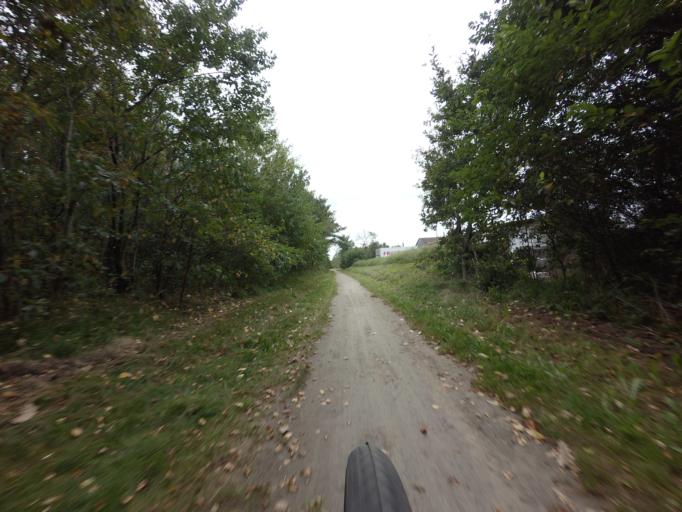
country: DK
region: Central Jutland
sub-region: Ikast-Brande Kommune
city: Brande
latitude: 55.8707
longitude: 9.0286
